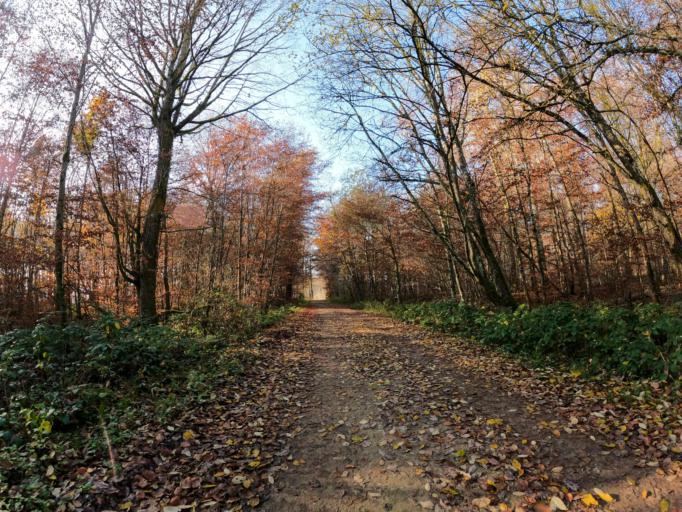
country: LU
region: Luxembourg
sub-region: Canton de Luxembourg
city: Olm
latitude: 49.6799
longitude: 5.9859
